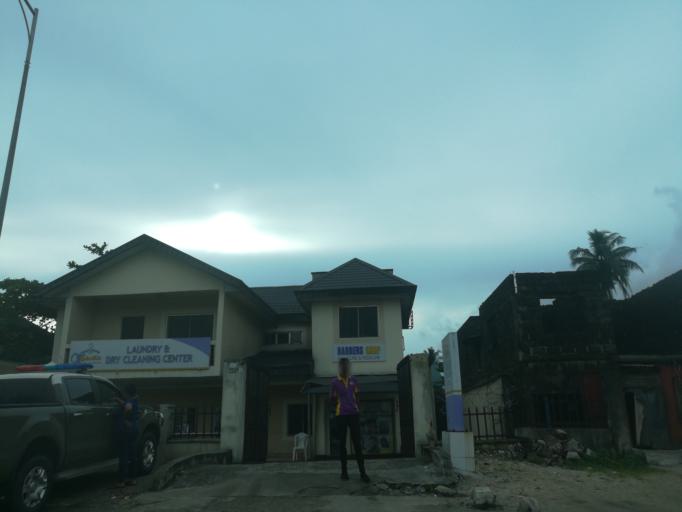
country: NG
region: Rivers
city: Port Harcourt
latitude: 4.8175
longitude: 6.9965
